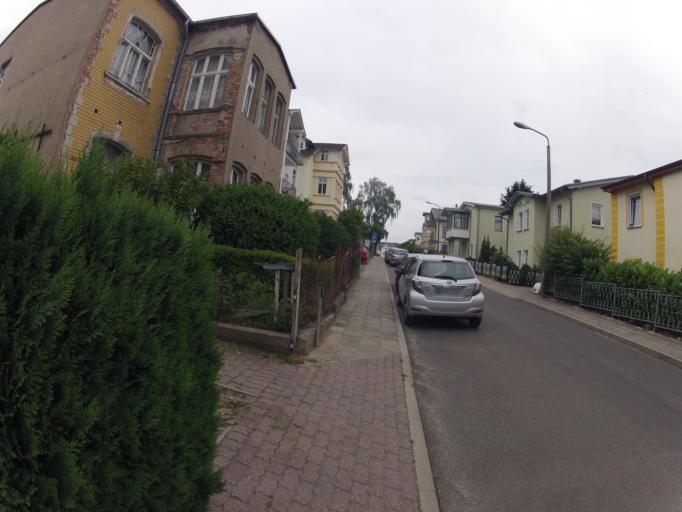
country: DE
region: Mecklenburg-Vorpommern
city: Seebad Heringsdorf
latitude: 53.9420
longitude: 14.1842
